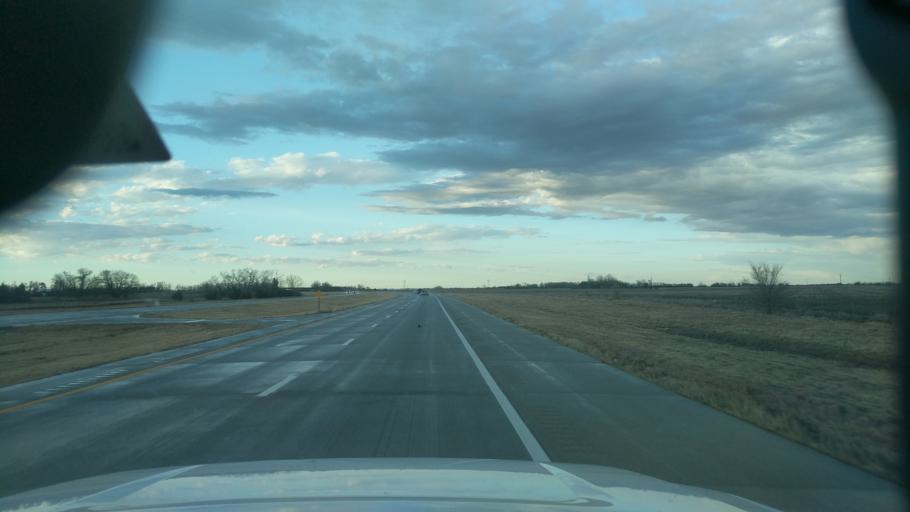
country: US
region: Kansas
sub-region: Harvey County
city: Hesston
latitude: 38.1656
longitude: -97.4375
